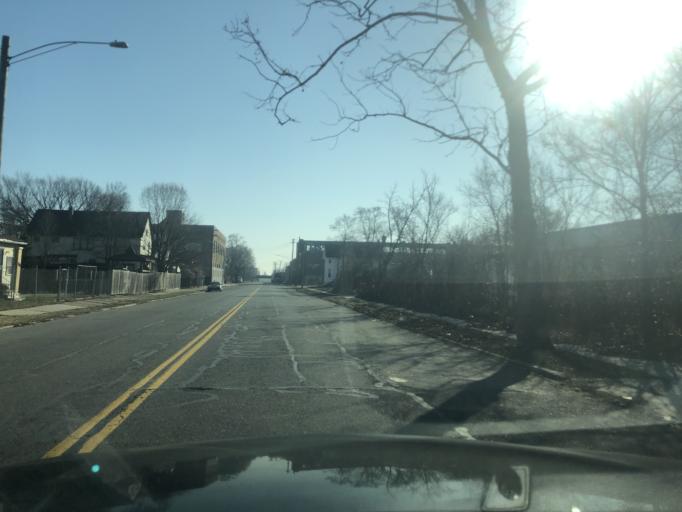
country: US
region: Michigan
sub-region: Wayne County
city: Detroit
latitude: 42.3354
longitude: -83.1043
